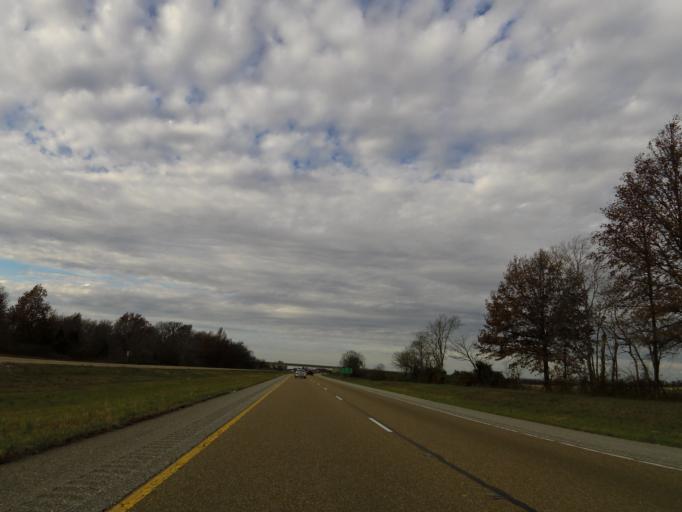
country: US
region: Illinois
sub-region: Clinton County
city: Wamac
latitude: 38.3895
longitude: -89.1863
